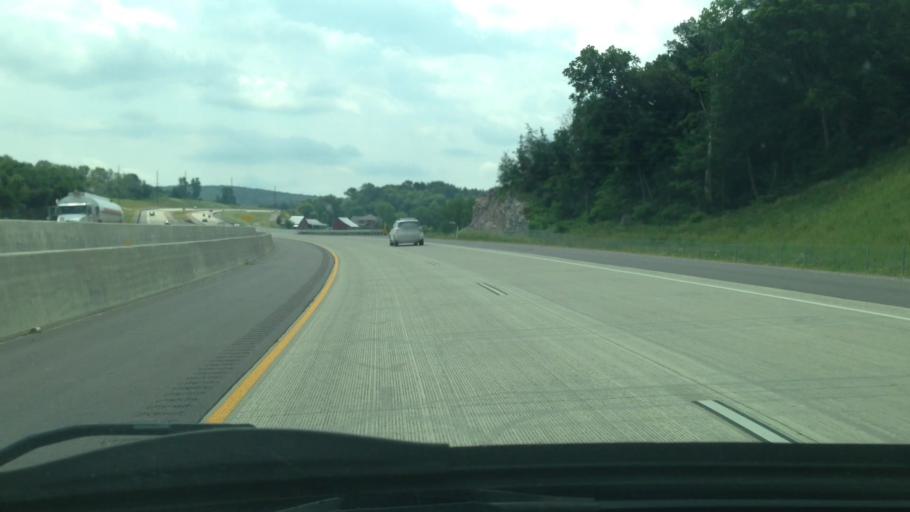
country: US
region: Wisconsin
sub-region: Sauk County
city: West Baraboo
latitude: 43.4344
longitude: -89.7778
